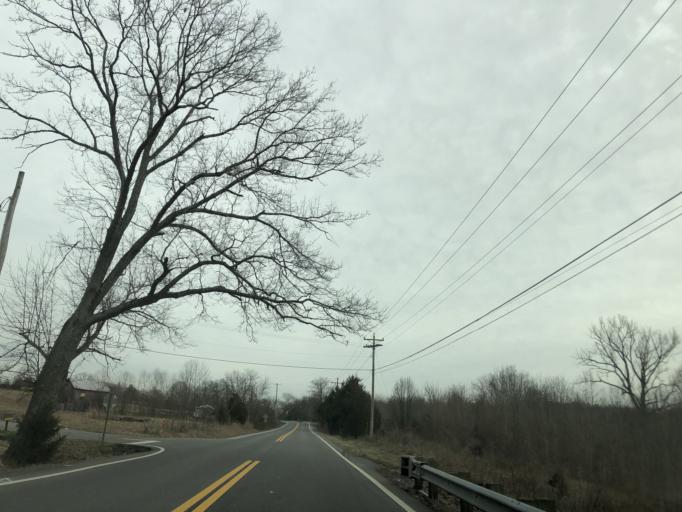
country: US
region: Tennessee
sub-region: Robertson County
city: Greenbrier
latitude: 36.4838
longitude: -86.7908
